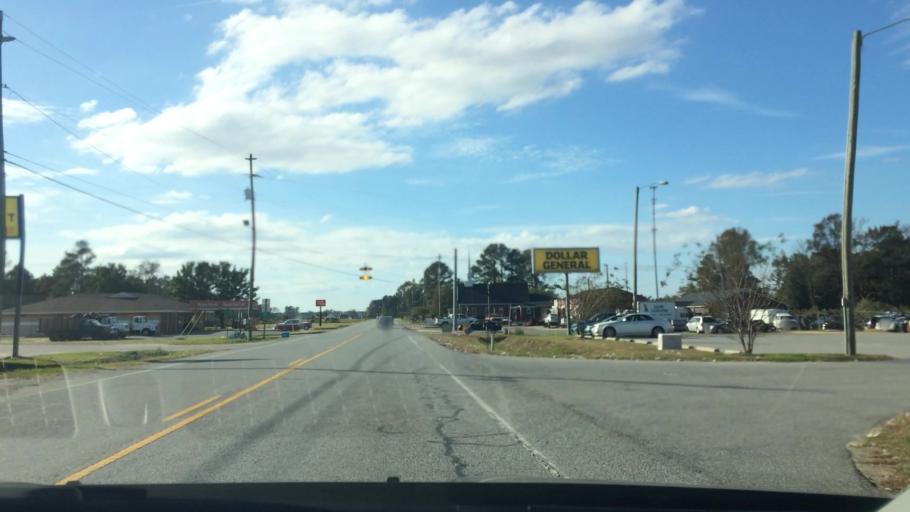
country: US
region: North Carolina
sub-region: Greene County
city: Snow Hill
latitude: 35.4403
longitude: -77.7908
